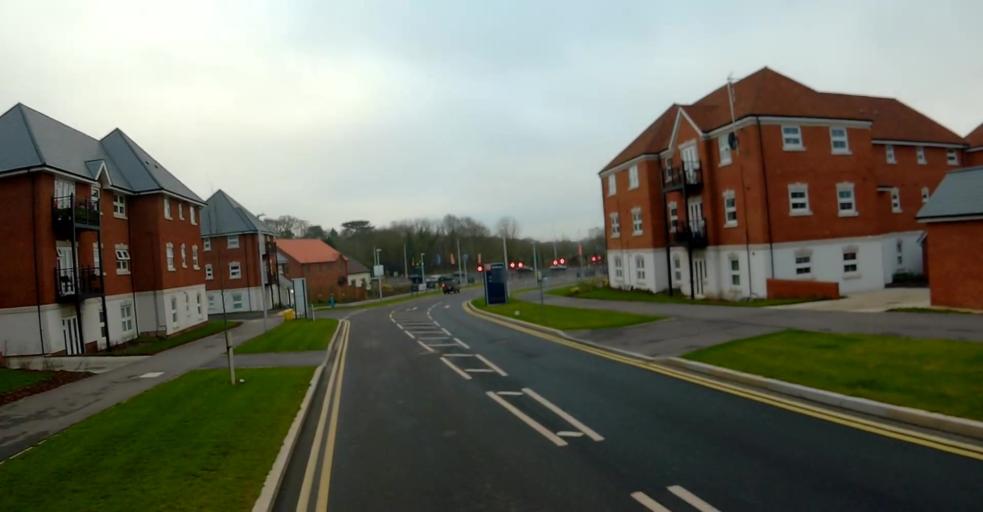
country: GB
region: England
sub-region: Bracknell Forest
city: Binfield
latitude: 51.4133
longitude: -0.8033
